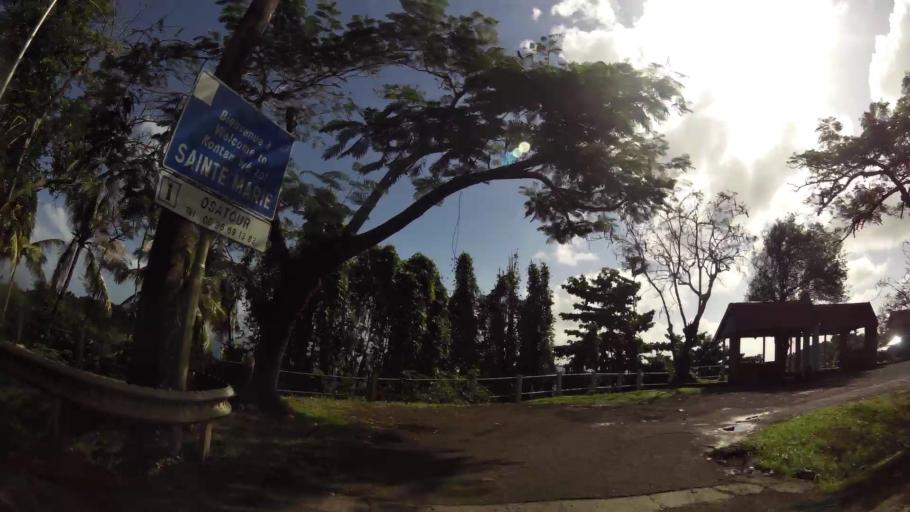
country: MQ
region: Martinique
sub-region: Martinique
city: Sainte-Marie
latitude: 14.7730
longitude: -60.9852
